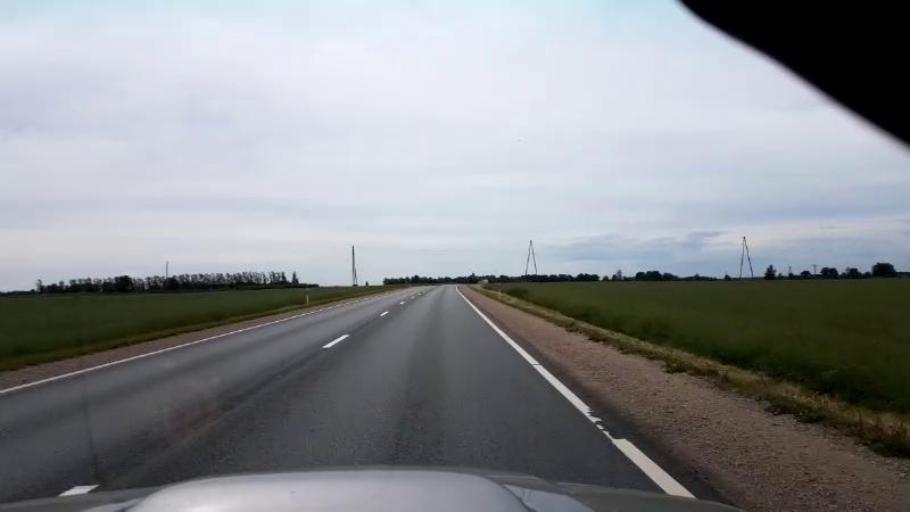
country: LV
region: Lecava
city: Iecava
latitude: 56.5394
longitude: 24.1728
